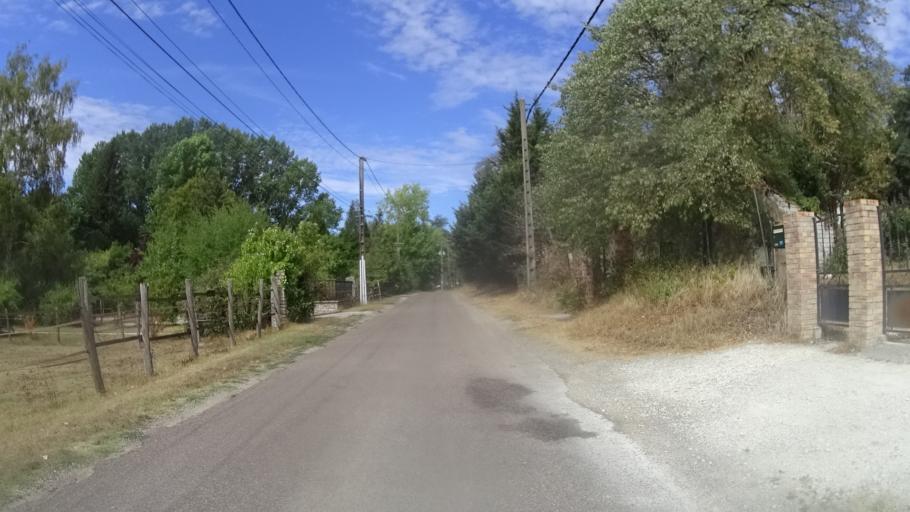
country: FR
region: Centre
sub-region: Departement du Loiret
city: Malesherbes
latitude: 48.2649
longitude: 2.4230
